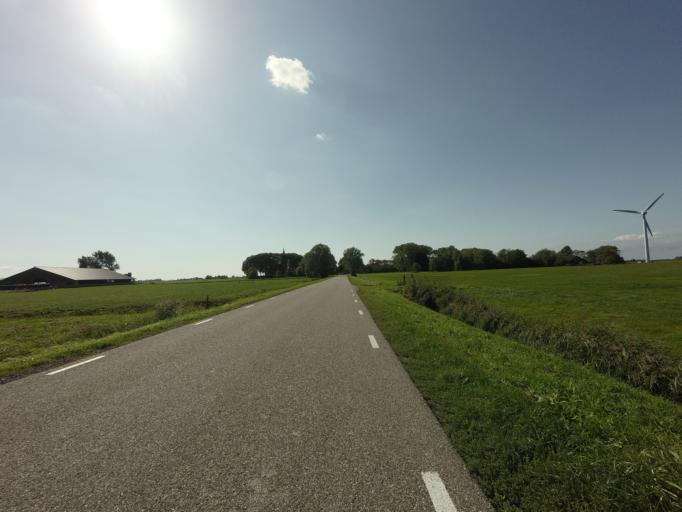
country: NL
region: Friesland
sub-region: Gemeente Littenseradiel
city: Makkum
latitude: 53.1141
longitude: 5.6799
